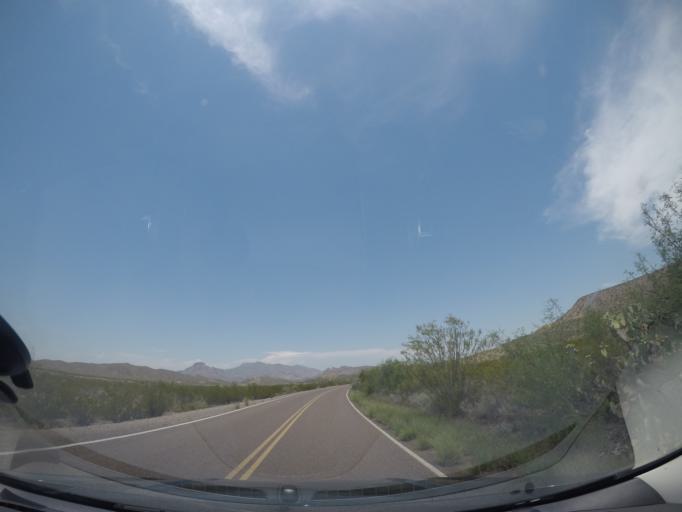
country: US
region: Texas
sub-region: Presidio County
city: Presidio
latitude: 29.3135
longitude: -103.3845
